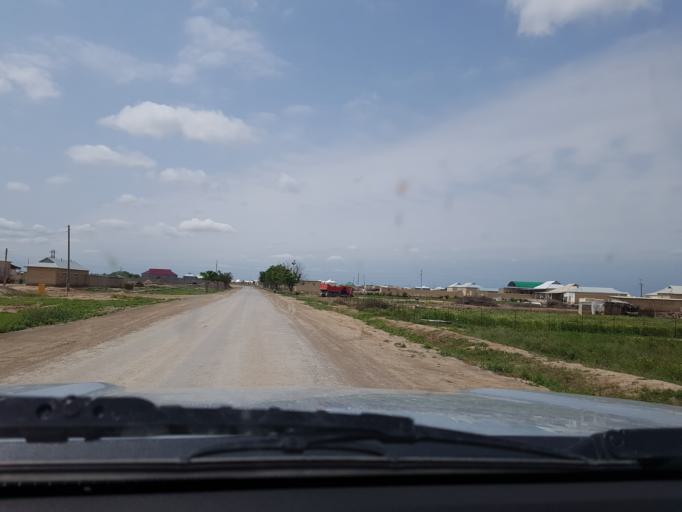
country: TM
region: Mary
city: Bayramaly
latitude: 37.6629
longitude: 62.1207
